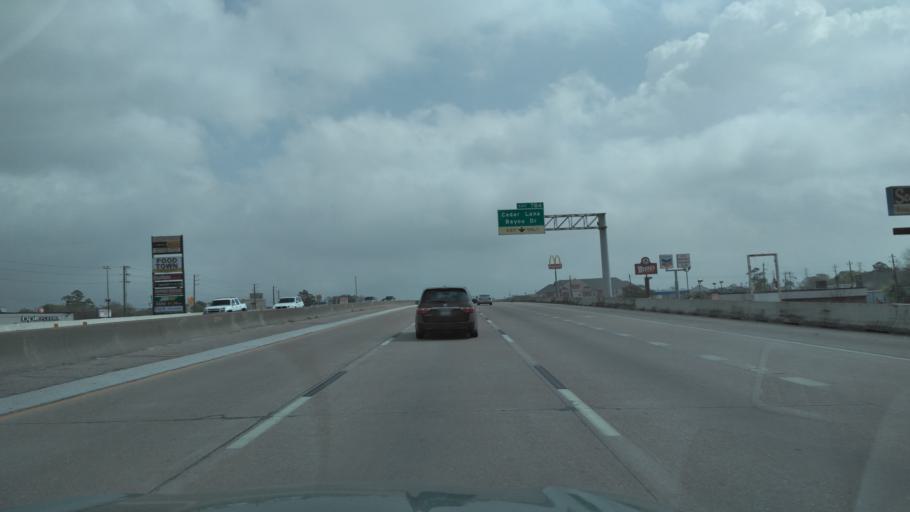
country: US
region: Texas
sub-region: Harris County
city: Channelview
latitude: 29.7774
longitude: -95.1268
